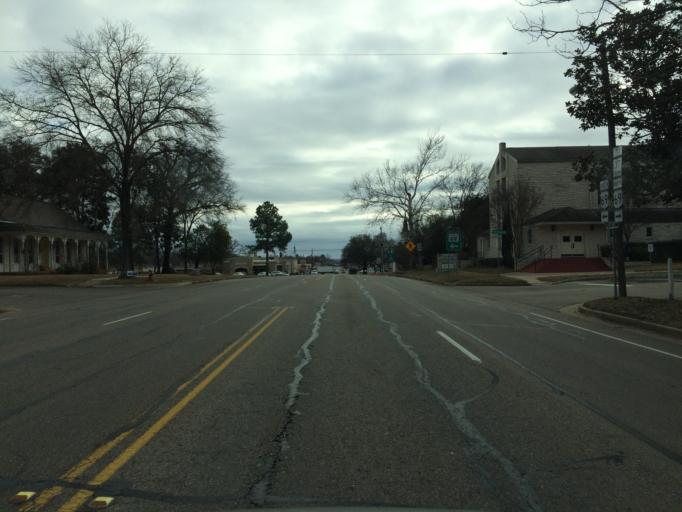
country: US
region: Texas
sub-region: Wood County
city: Mineola
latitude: 32.6666
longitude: -95.4872
